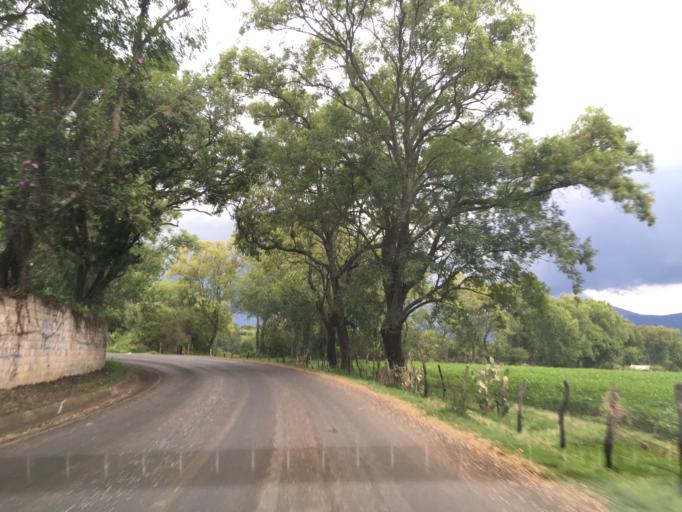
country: MX
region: Michoacan
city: Acuitzio del Canje
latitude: 19.5581
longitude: -101.2722
